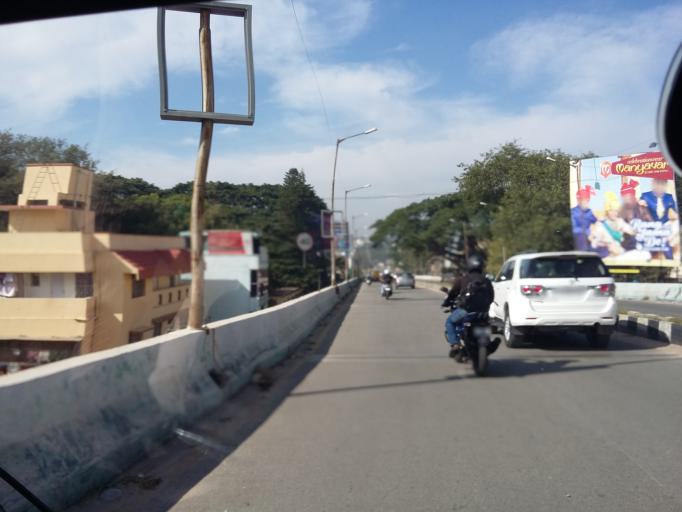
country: IN
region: Karnataka
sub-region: Bangalore Urban
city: Bangalore
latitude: 12.9979
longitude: 77.6219
